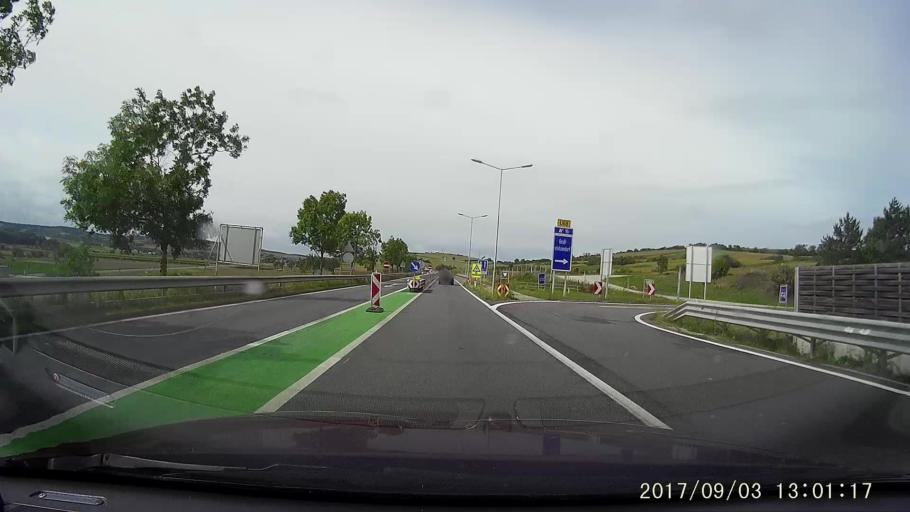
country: AT
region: Lower Austria
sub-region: Politischer Bezirk Hollabrunn
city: Gollersdorf
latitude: 48.5064
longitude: 16.0975
